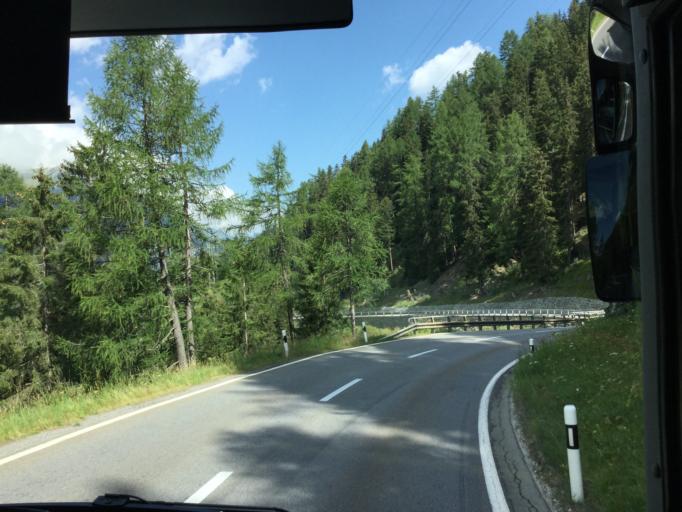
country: CH
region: Grisons
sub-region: Albula District
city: Tiefencastel
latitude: 46.5116
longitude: 9.6334
